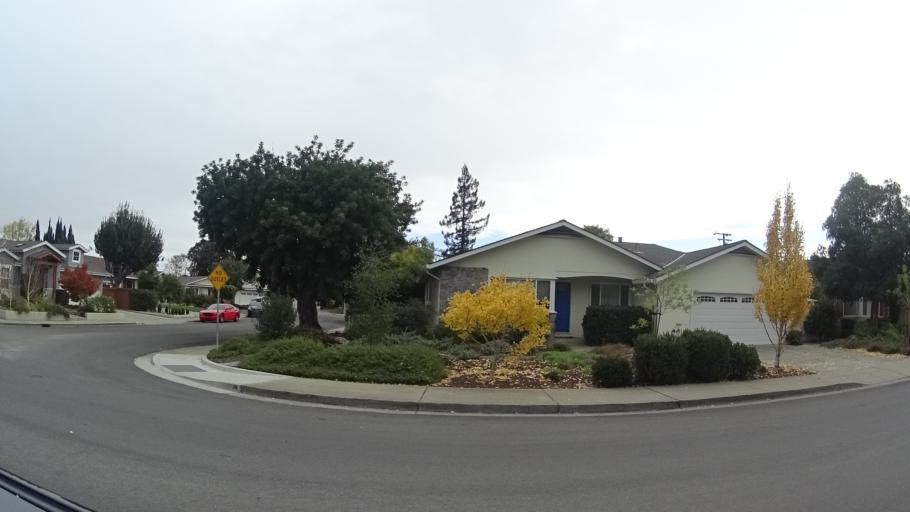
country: US
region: California
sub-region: Santa Clara County
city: Sunnyvale
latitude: 37.3632
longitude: -122.0182
